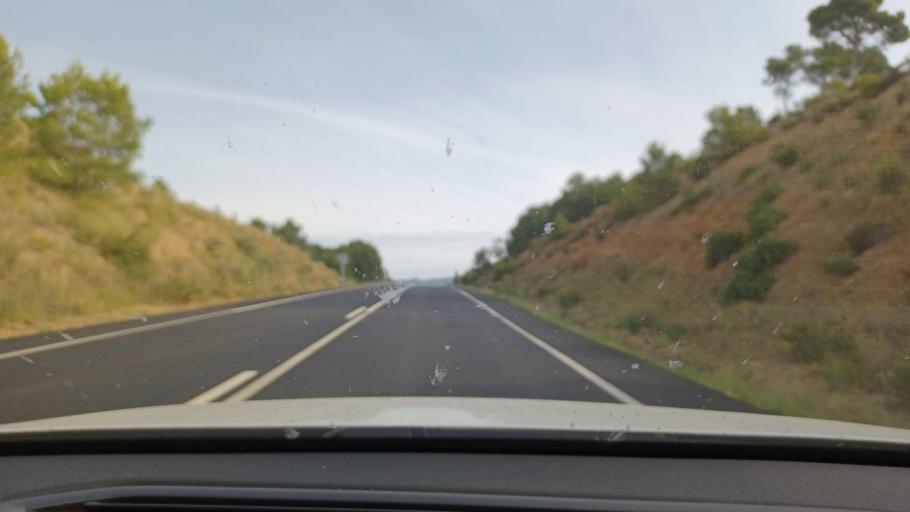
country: ES
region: Catalonia
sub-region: Provincia de Tarragona
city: Benifallet
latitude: 40.9978
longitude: 0.5154
